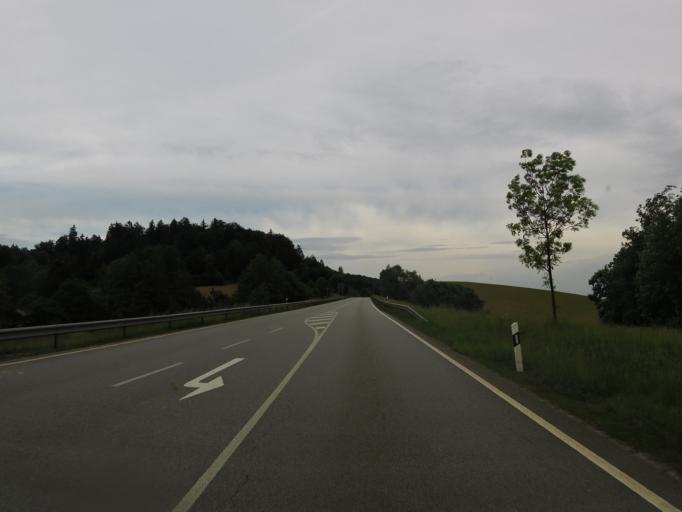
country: DE
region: Bavaria
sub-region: Lower Bavaria
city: Roehrnbach
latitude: 48.7721
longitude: 13.5076
